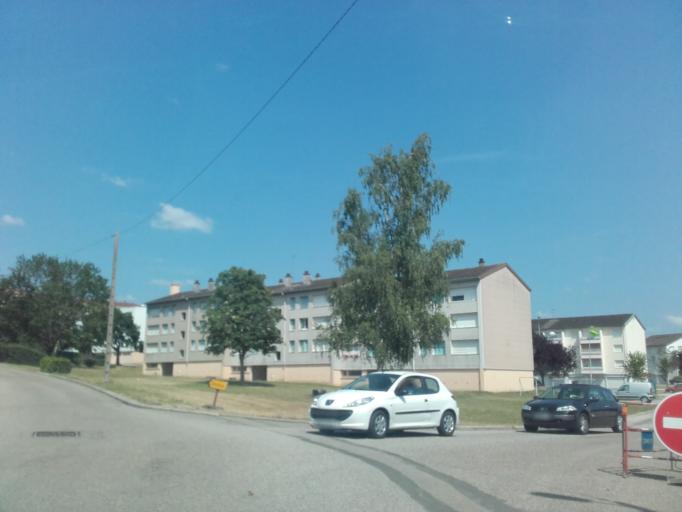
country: FR
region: Rhone-Alpes
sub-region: Departement de l'Ain
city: Chalamont
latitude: 45.9946
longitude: 5.1716
